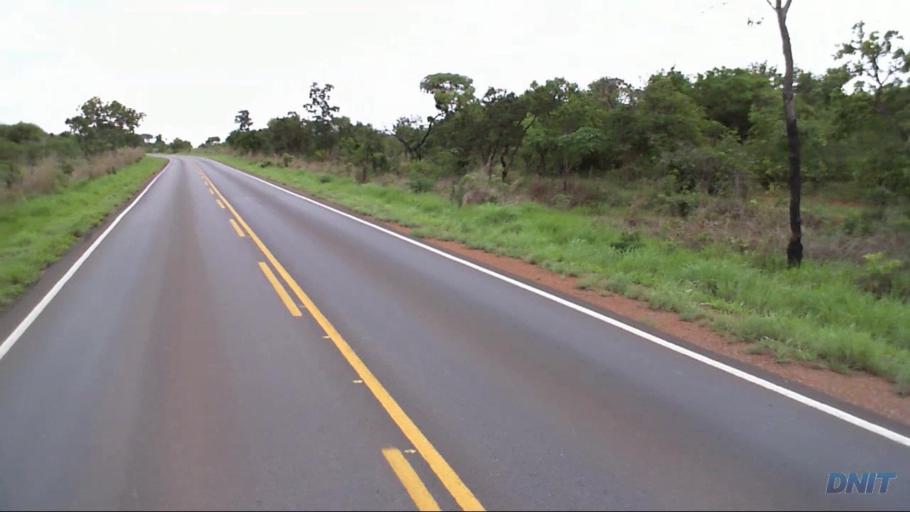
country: BR
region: Goias
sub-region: Padre Bernardo
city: Padre Bernardo
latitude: -15.3955
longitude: -48.2012
